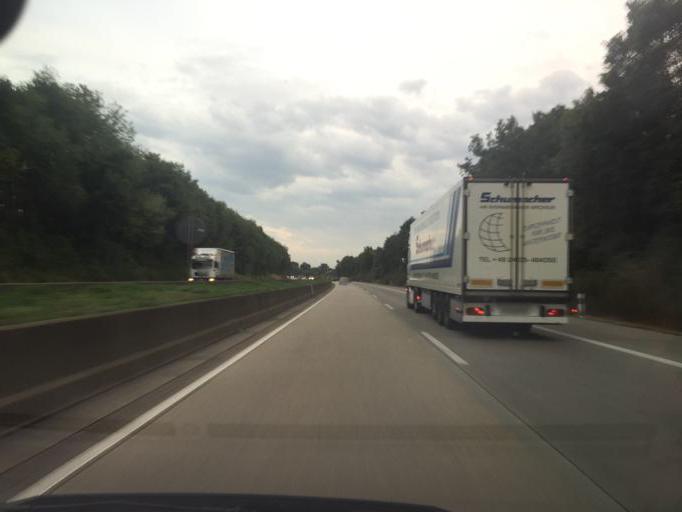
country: DE
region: North Rhine-Westphalia
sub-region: Regierungsbezirk Koln
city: Titz
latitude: 51.0210
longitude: 6.4861
